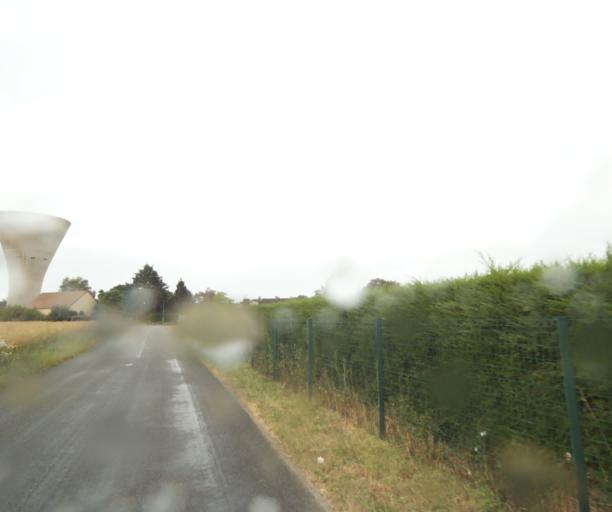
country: FR
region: Ile-de-France
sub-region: Departement de Seine-et-Marne
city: Perthes
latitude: 48.4828
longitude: 2.5492
